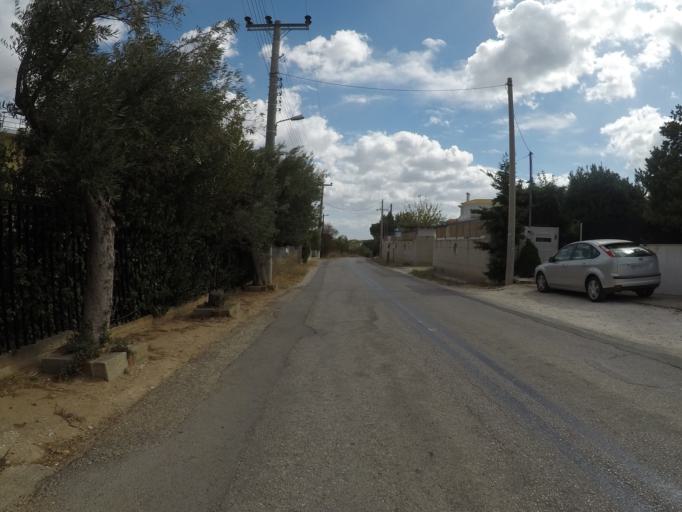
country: GR
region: Attica
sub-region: Nomarchia Anatolikis Attikis
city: Agios Dimitrios Kropias
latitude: 37.8102
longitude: 23.8683
